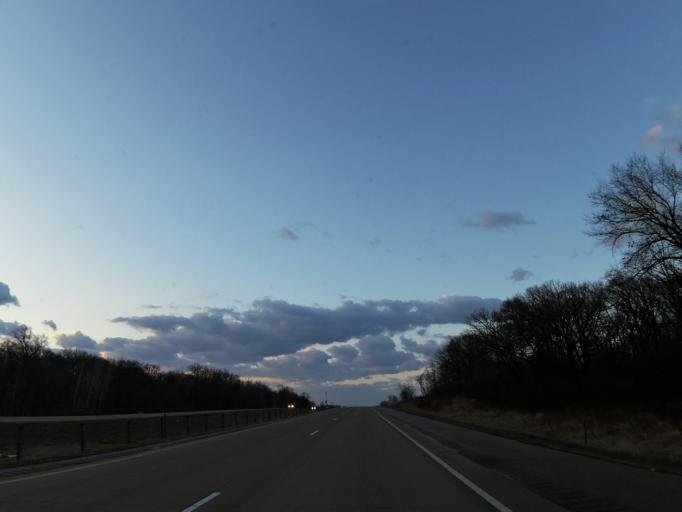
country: US
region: Minnesota
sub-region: Scott County
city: Elko New Market
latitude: 44.5277
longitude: -93.2979
